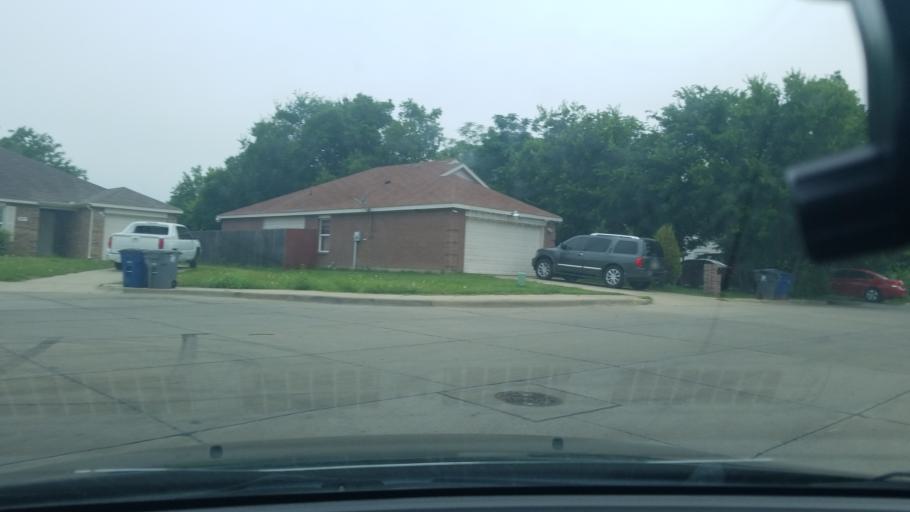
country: US
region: Texas
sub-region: Dallas County
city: Balch Springs
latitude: 32.7599
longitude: -96.6766
